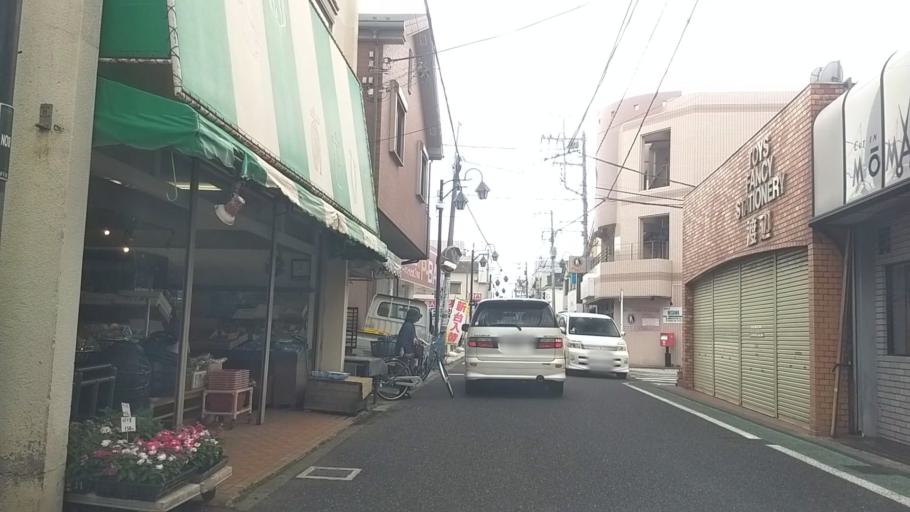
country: JP
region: Kanagawa
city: Fujisawa
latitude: 35.3395
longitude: 139.4514
